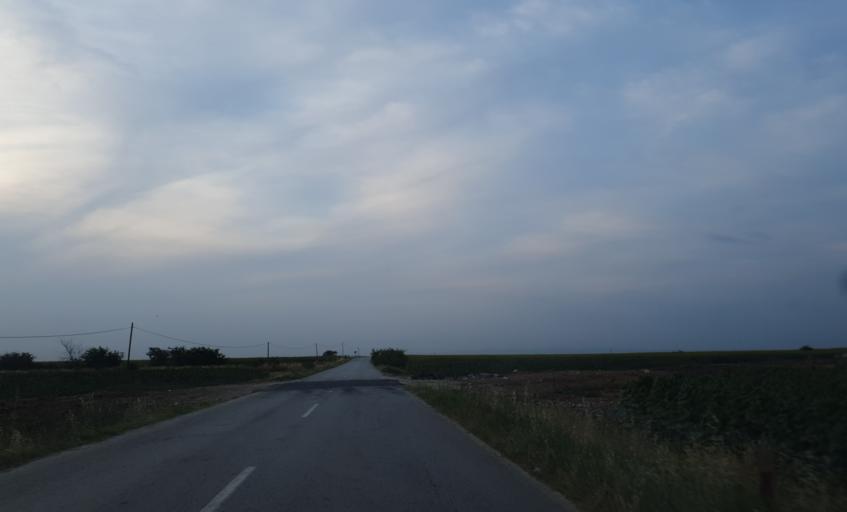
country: TR
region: Kirklareli
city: Buyukkaristiran
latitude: 41.3327
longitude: 27.6052
